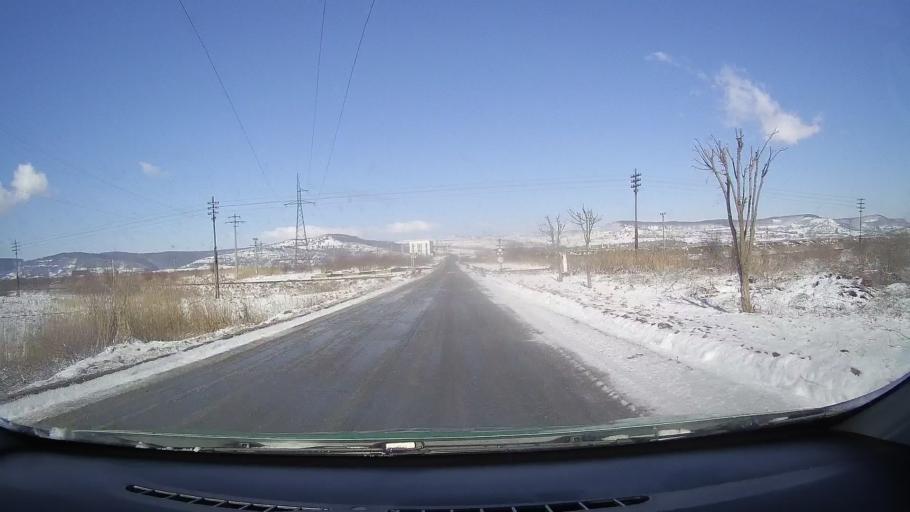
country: RO
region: Sibiu
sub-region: Comuna Avrig
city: Avrig
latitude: 45.7396
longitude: 24.3923
